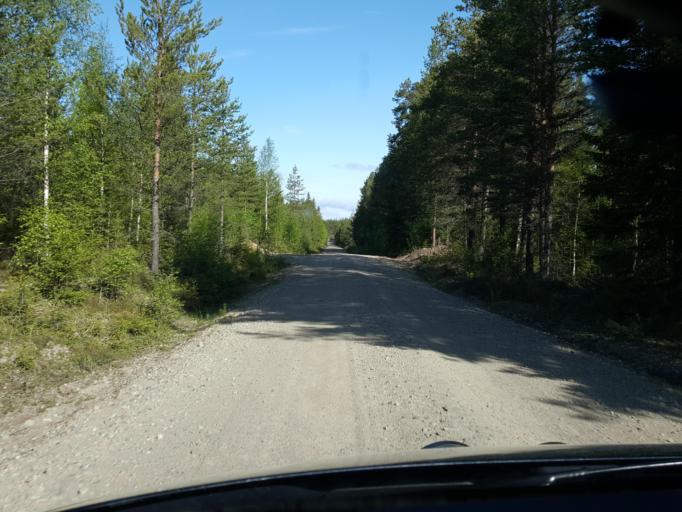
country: SE
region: Vaesternorrland
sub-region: Ange Kommun
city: Ange
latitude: 62.1868
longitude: 15.6020
